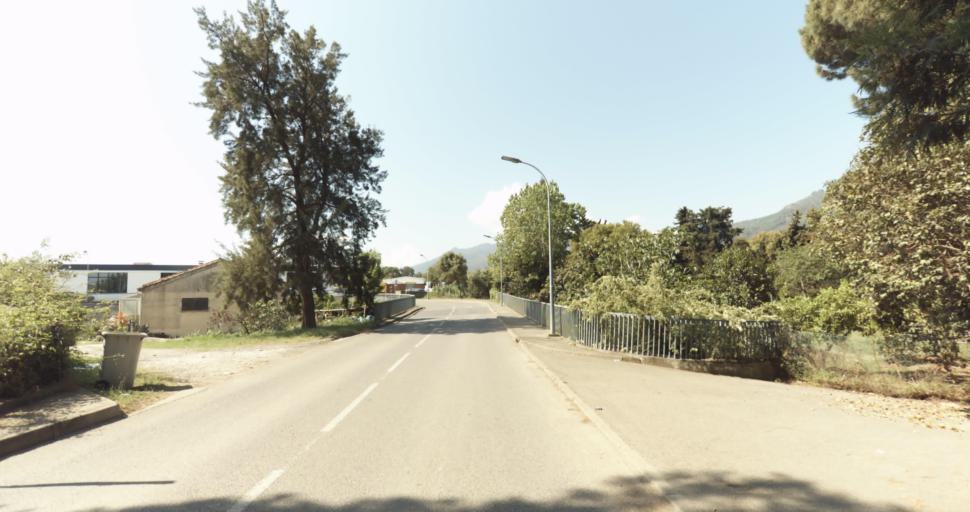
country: FR
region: Corsica
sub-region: Departement de la Haute-Corse
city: Biguglia
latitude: 42.6294
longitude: 9.4366
